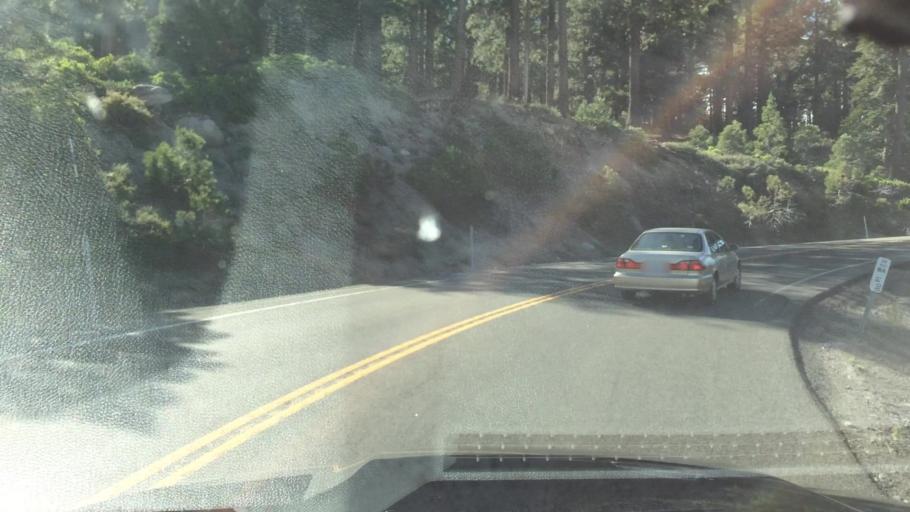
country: US
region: Nevada
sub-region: Washoe County
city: Incline Village
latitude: 39.3390
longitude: -119.8658
